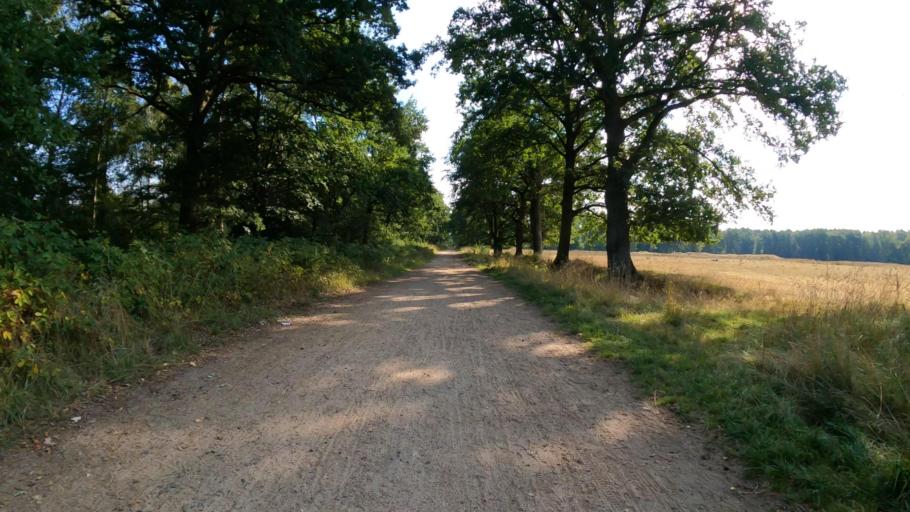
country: DE
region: Schleswig-Holstein
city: Bornsen
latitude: 53.4991
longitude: 10.2845
